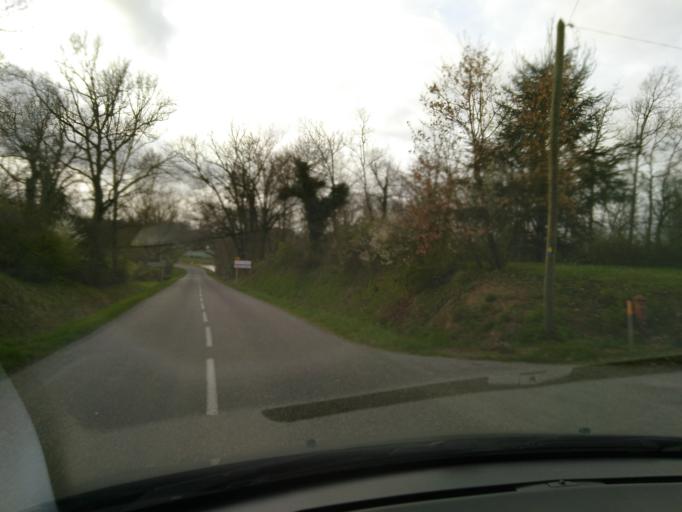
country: FR
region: Midi-Pyrenees
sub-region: Departement du Tarn-et-Garonne
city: Finhan
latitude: 43.8949
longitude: 1.1411
